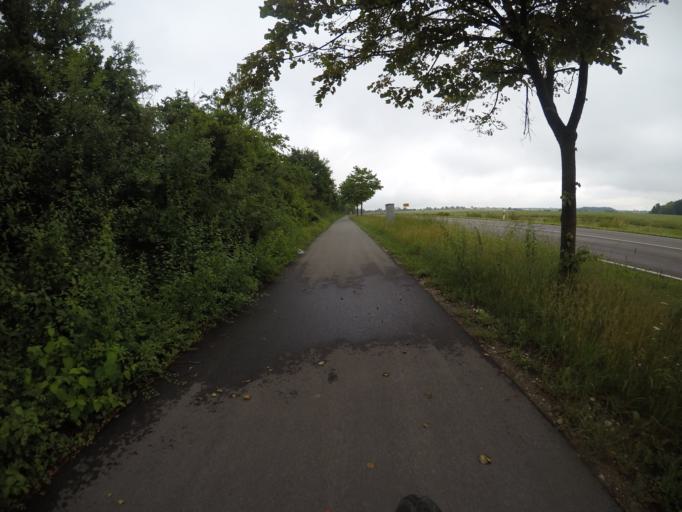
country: DE
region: Baden-Wuerttemberg
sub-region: Tuebingen Region
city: Ulm
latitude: 48.4312
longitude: 9.9856
